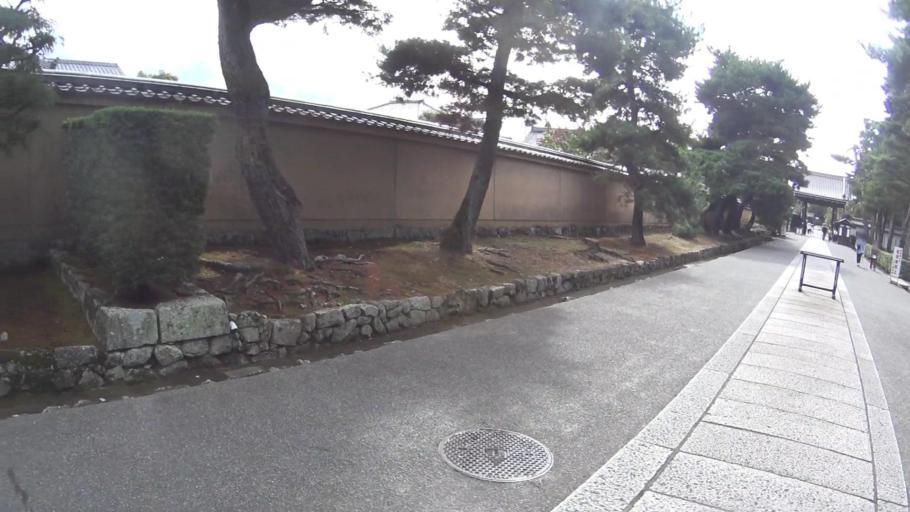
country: JP
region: Kyoto
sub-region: Kyoto-shi
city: Kamigyo-ku
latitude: 35.0341
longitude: 135.7612
